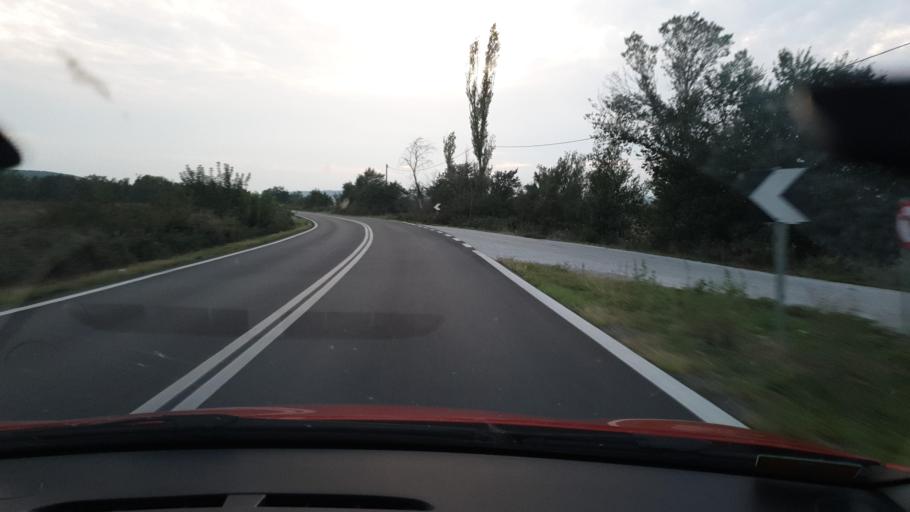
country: GR
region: Central Macedonia
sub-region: Nomos Kilkis
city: Kristoni
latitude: 41.0038
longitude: 22.7872
